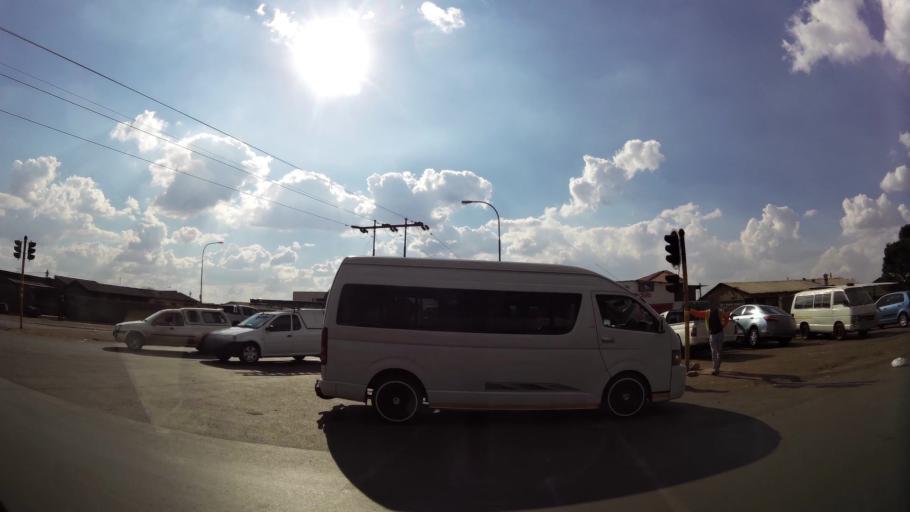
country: ZA
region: Gauteng
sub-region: City of Johannesburg Metropolitan Municipality
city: Soweto
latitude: -26.2253
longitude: 27.8584
